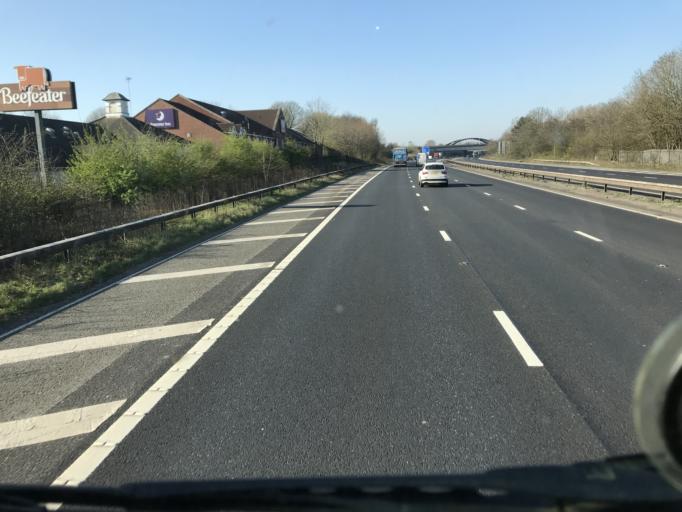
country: GB
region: England
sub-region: Borough of Halton
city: Halton
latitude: 53.3149
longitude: -2.6641
